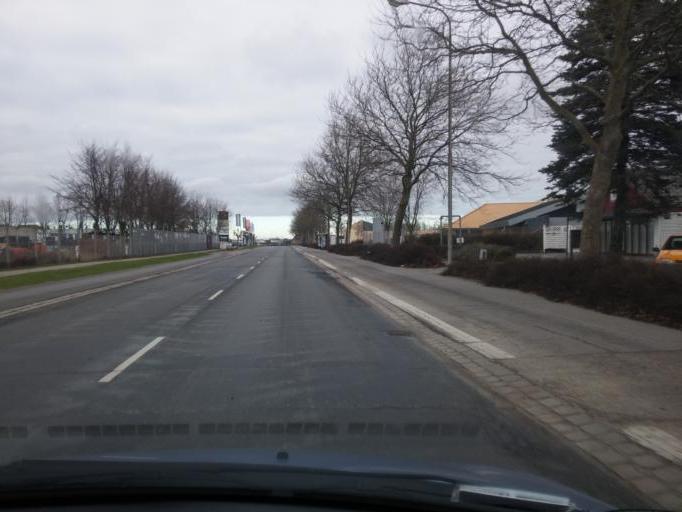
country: DK
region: South Denmark
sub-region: Odense Kommune
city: Neder Holluf
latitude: 55.3881
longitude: 10.4398
